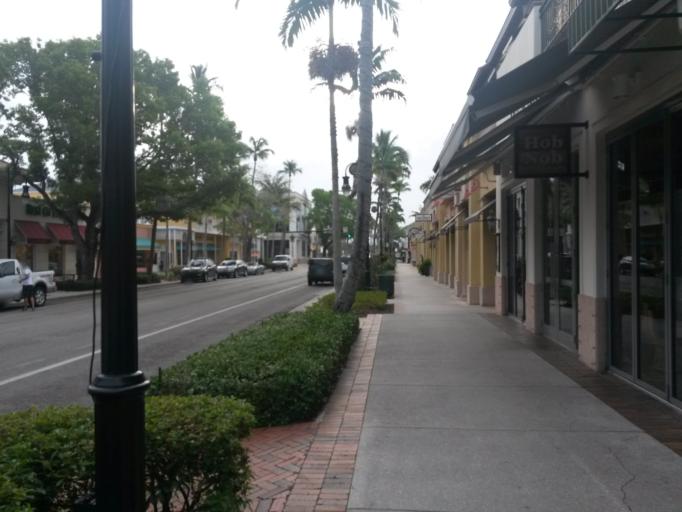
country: US
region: Florida
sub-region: Collier County
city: Naples
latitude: 26.1415
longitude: -81.7972
